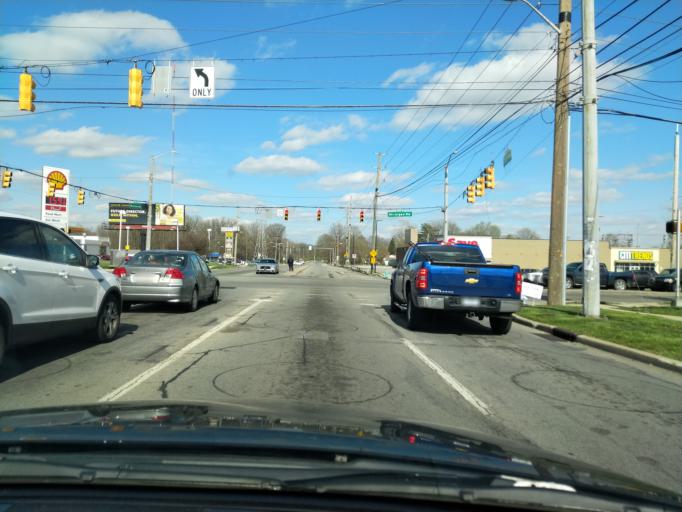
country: US
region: Indiana
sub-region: Marion County
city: Meridian Hills
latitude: 39.8846
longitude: -86.2101
